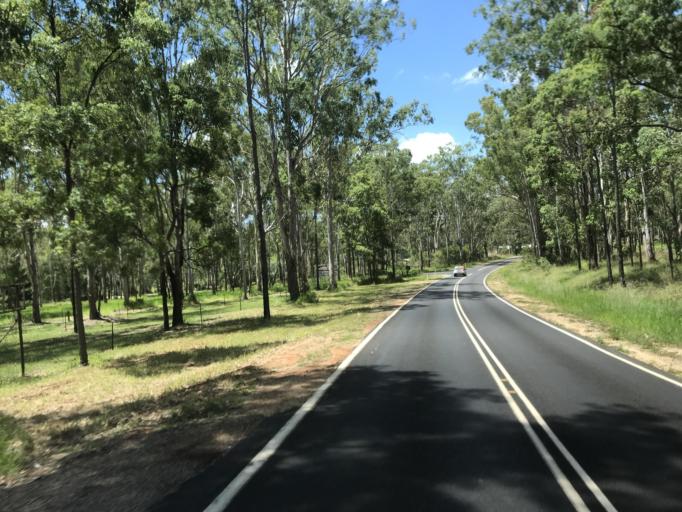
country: AU
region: Queensland
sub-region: Tablelands
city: Atherton
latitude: -17.4187
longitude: 145.3930
